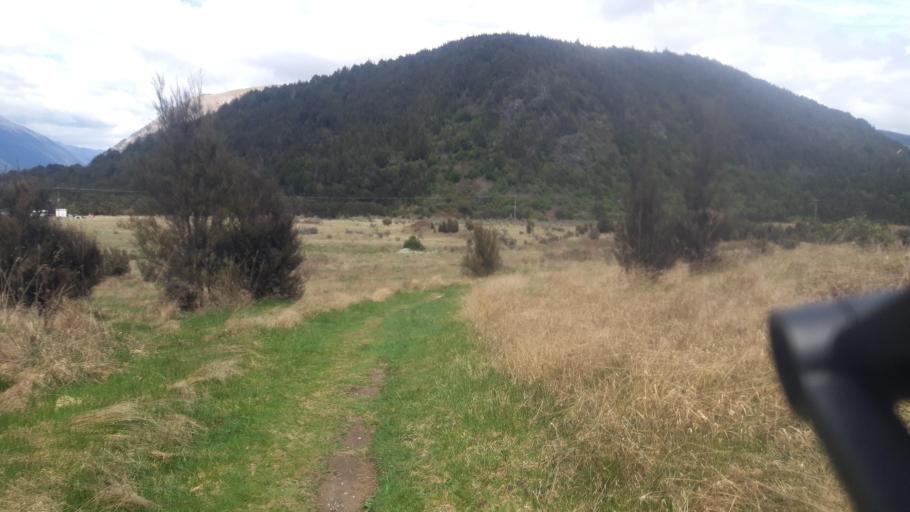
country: NZ
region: Tasman
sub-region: Tasman District
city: Wakefield
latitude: -41.7933
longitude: 172.8391
